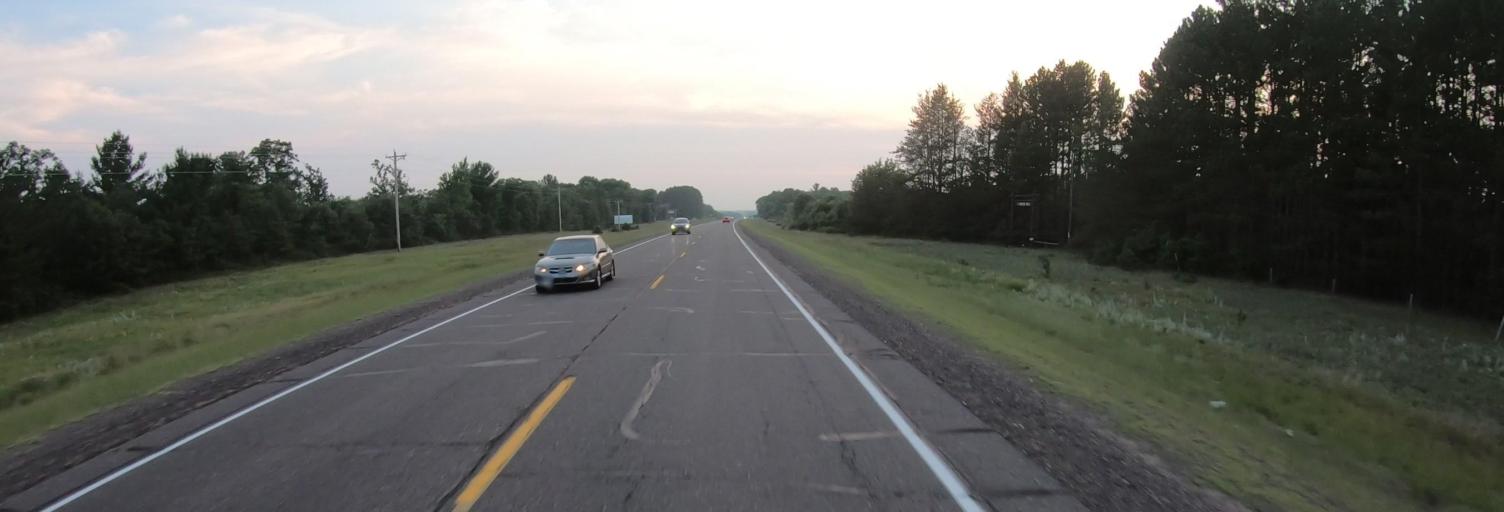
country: US
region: Wisconsin
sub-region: Burnett County
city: Grantsburg
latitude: 45.7730
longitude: -92.7584
